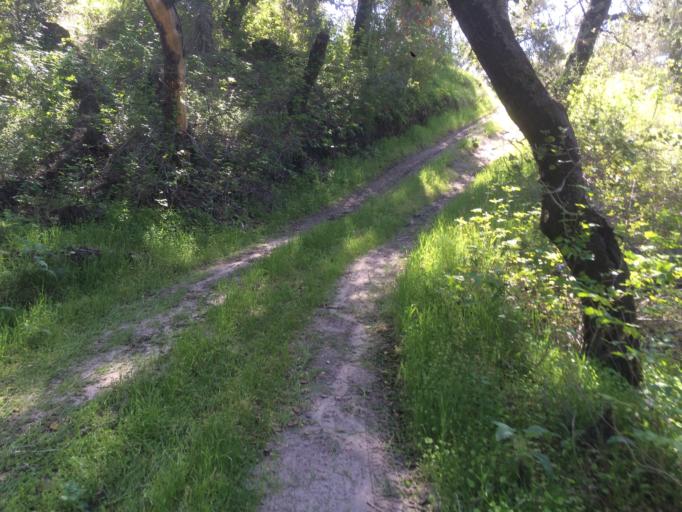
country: US
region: California
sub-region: San Luis Obispo County
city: Nipomo
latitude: 35.1793
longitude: -120.3937
